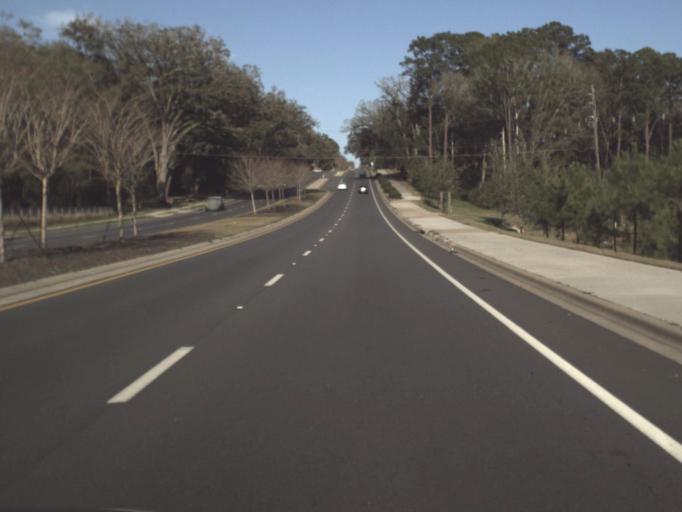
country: US
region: Florida
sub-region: Leon County
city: Tallahassee
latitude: 30.4686
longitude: -84.2041
